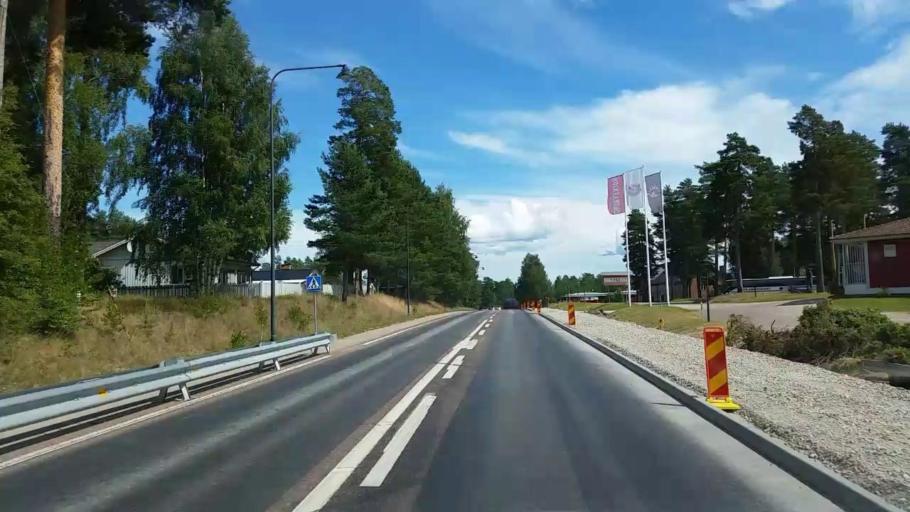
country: SE
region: Dalarna
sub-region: Rattviks Kommun
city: Vikarbyn
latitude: 61.1685
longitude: 15.1379
